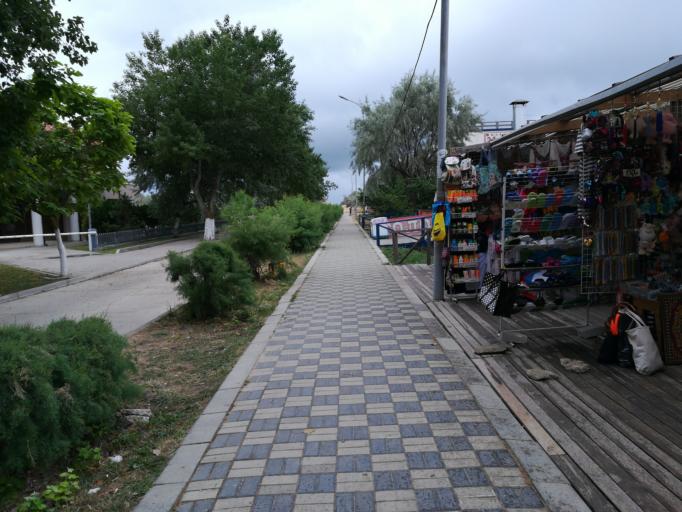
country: RU
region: Krasnodarskiy
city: Vityazevo
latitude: 44.9886
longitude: 37.2455
